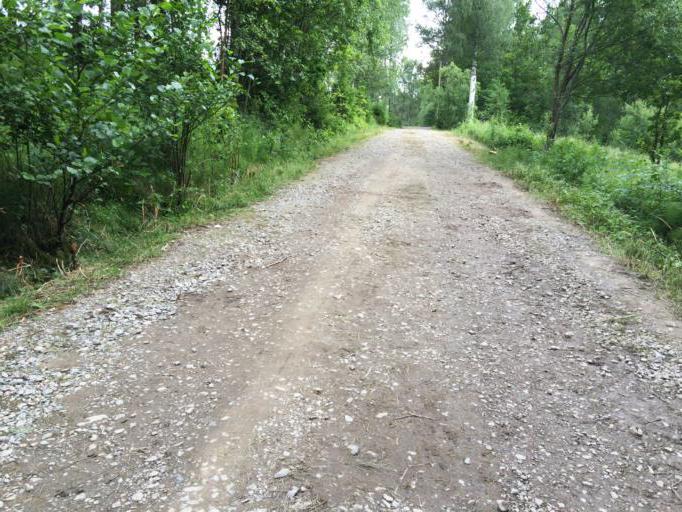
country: SE
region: Vaestra Goetaland
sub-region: Fargelanda Kommun
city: Faergelanda
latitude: 58.5838
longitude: 12.0853
